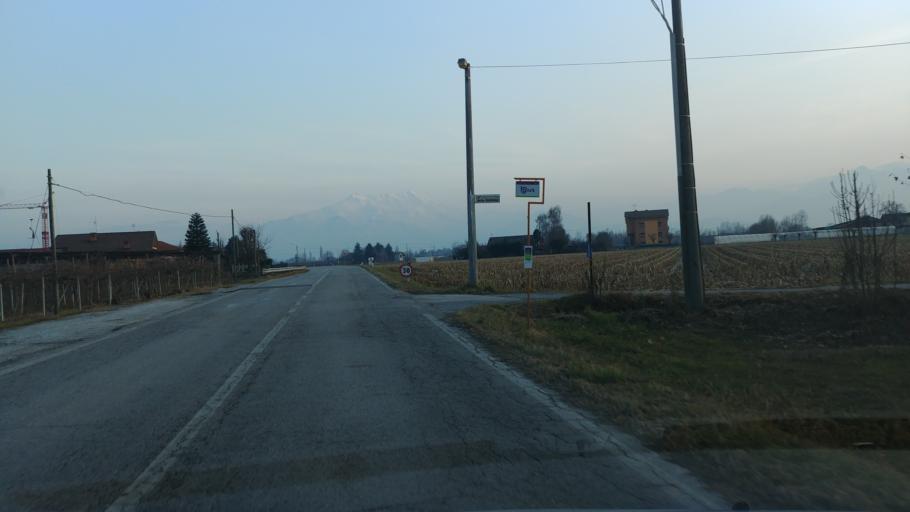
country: IT
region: Piedmont
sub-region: Provincia di Cuneo
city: Roata Rossi
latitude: 44.4172
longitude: 7.5101
